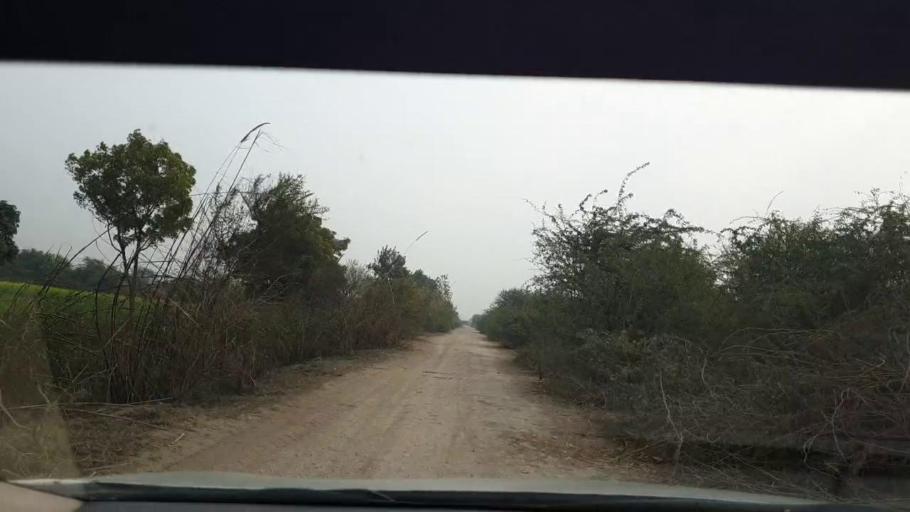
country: PK
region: Sindh
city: Berani
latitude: 25.8637
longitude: 68.8320
